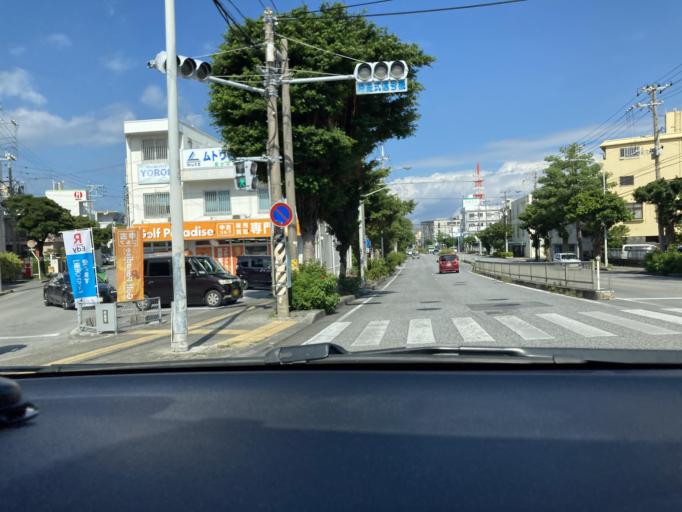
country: JP
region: Okinawa
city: Naha-shi
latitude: 26.2381
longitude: 127.6956
